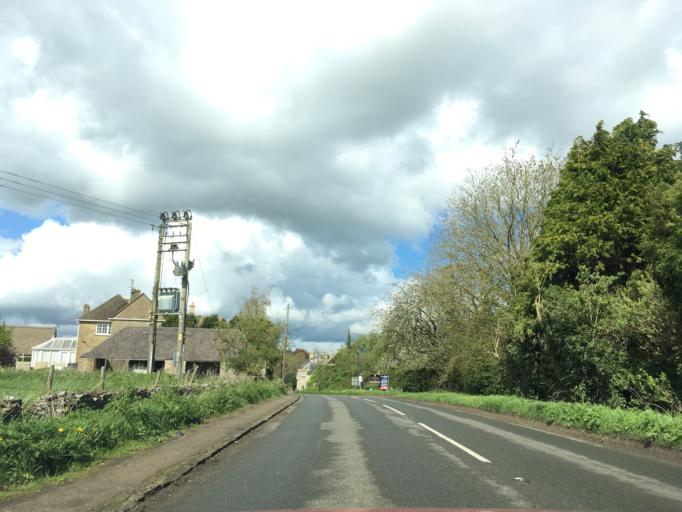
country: GB
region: England
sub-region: Gloucestershire
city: Tetbury
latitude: 51.6319
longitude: -2.1640
